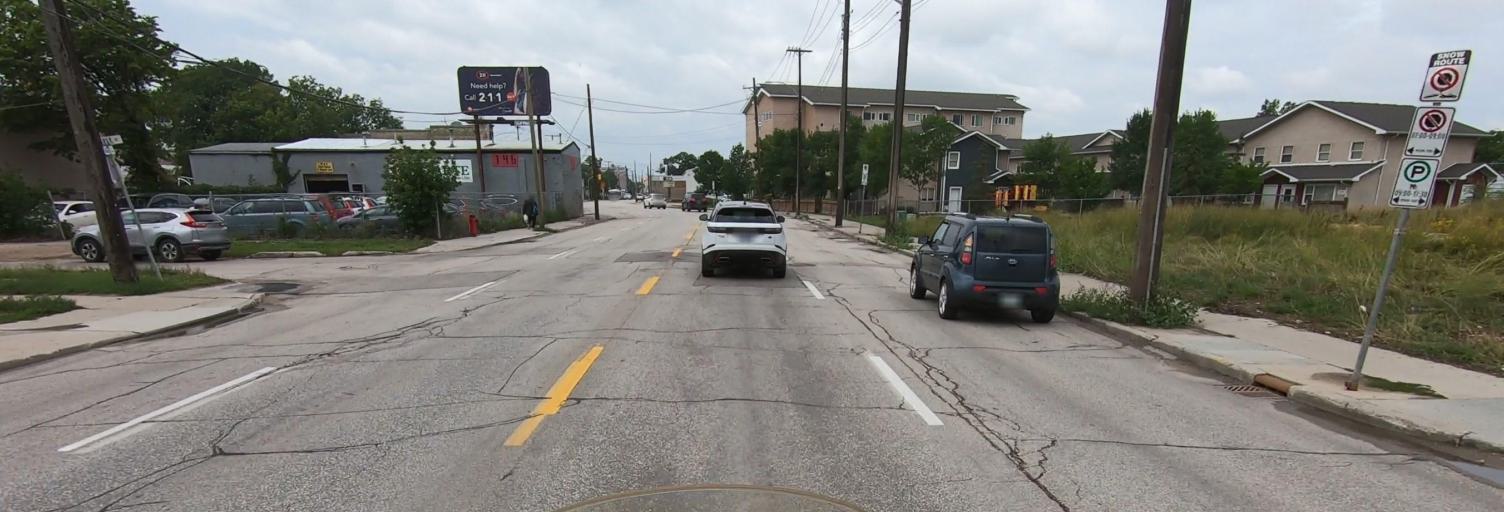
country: CA
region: Manitoba
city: Winnipeg
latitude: 49.9038
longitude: -97.1280
